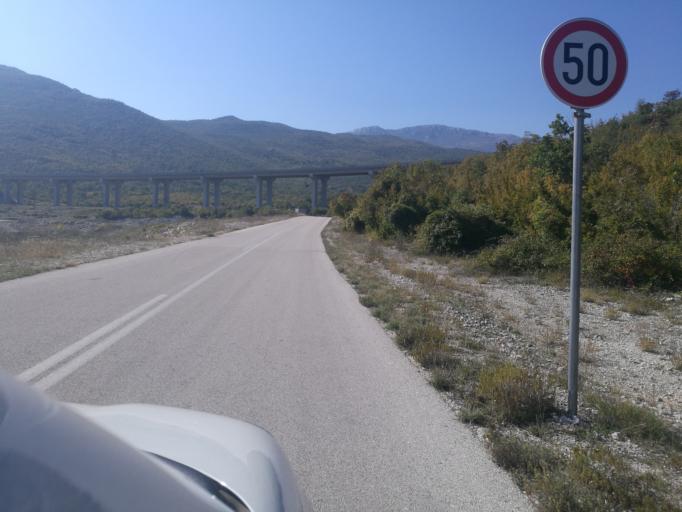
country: HR
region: Splitsko-Dalmatinska
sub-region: Grad Omis
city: Omis
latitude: 43.5193
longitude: 16.7415
